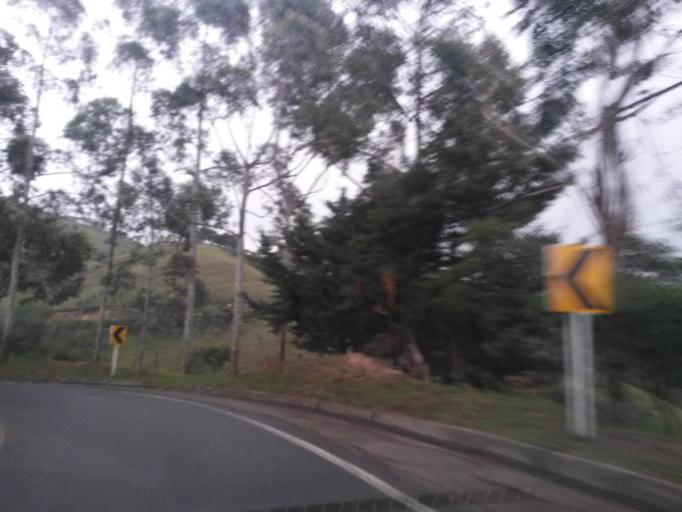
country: CO
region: Cauca
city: Popayan
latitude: 2.4067
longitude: -76.5042
